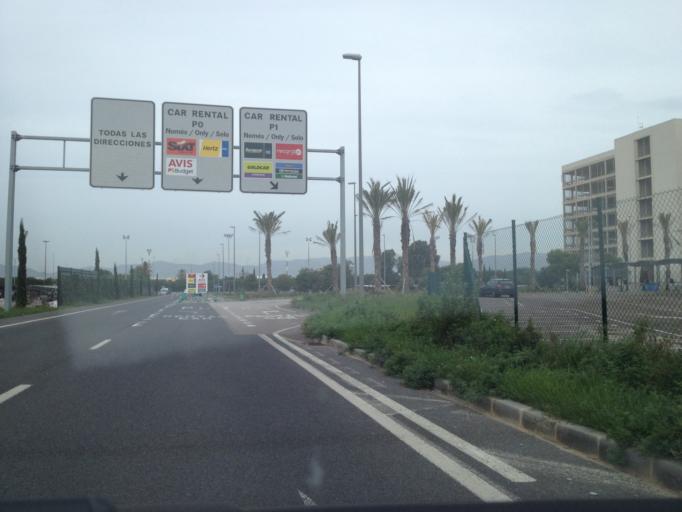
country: ES
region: Balearic Islands
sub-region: Illes Balears
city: s'Arenal
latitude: 39.5449
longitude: 2.7270
